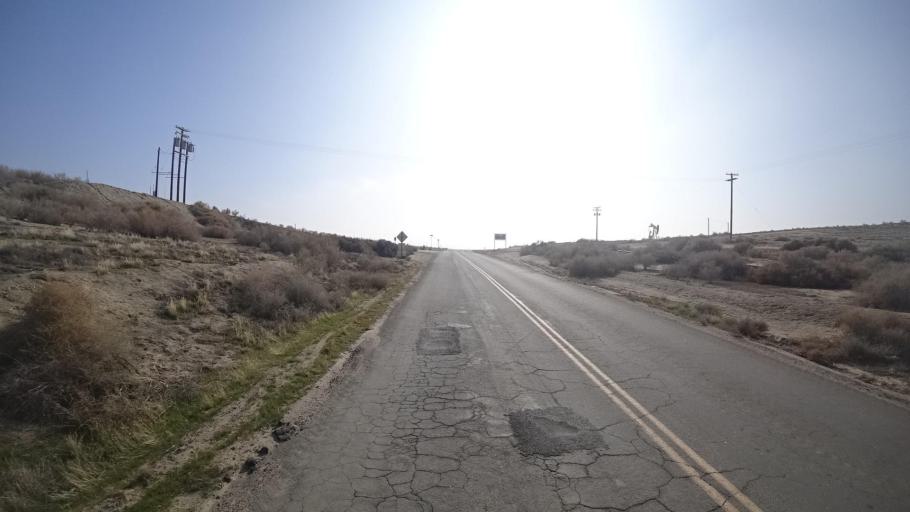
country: US
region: California
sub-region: Kern County
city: Ford City
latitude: 35.1637
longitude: -119.4208
